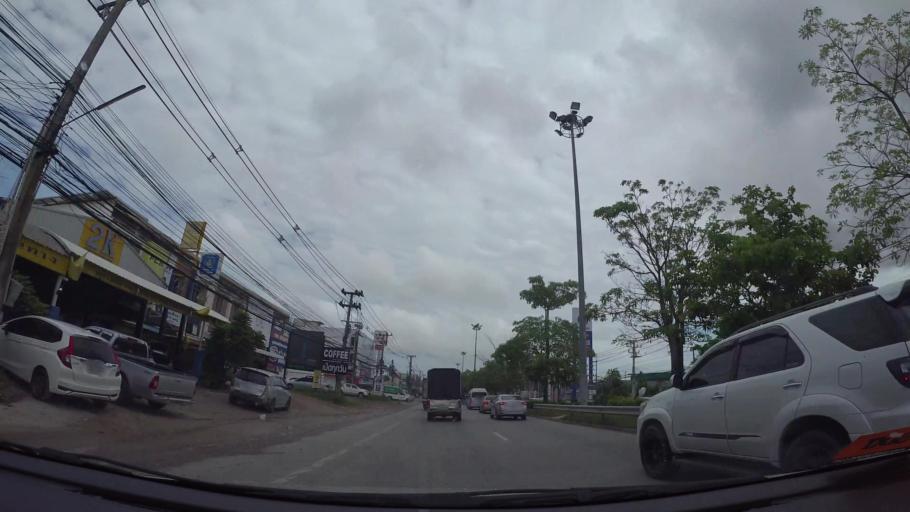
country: TH
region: Rayong
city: Rayong
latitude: 12.7008
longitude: 101.1893
